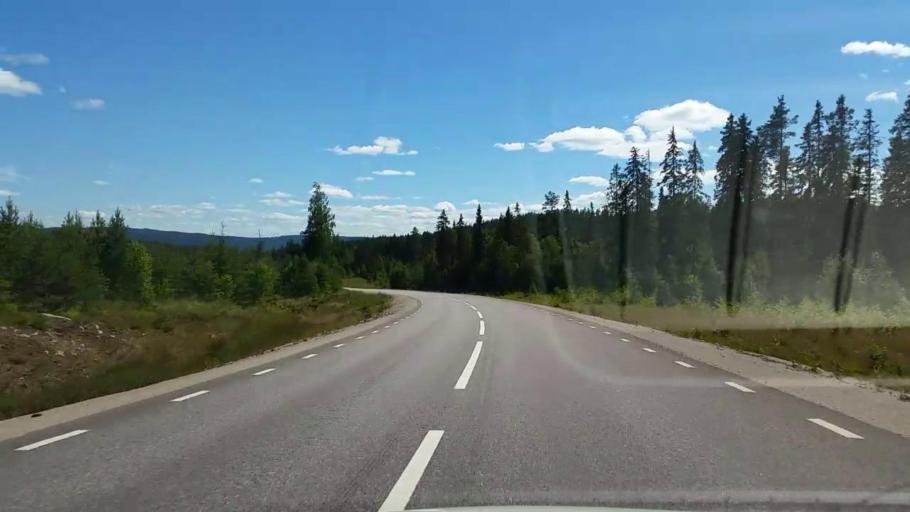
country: SE
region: Gaevleborg
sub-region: Bollnas Kommun
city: Vittsjo
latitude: 61.0694
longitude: 15.7957
